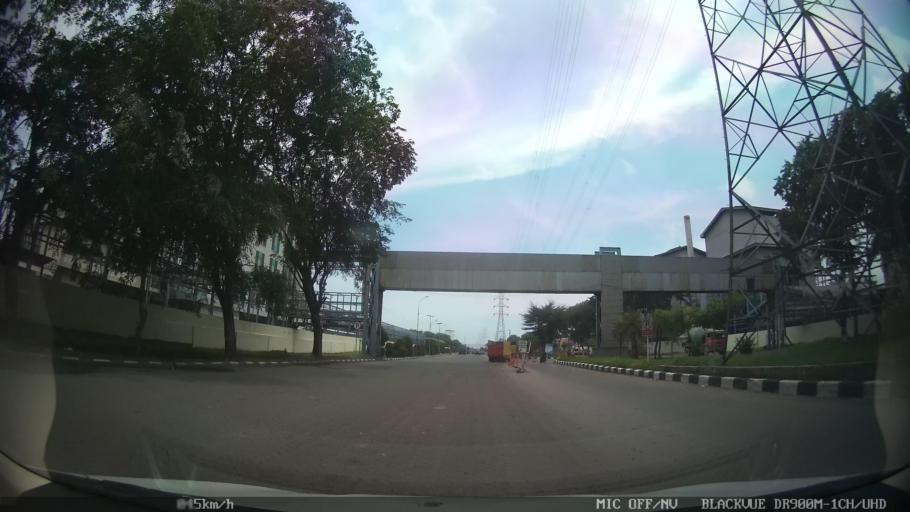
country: ID
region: North Sumatra
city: Labuhan Deli
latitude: 3.6727
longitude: 98.6848
